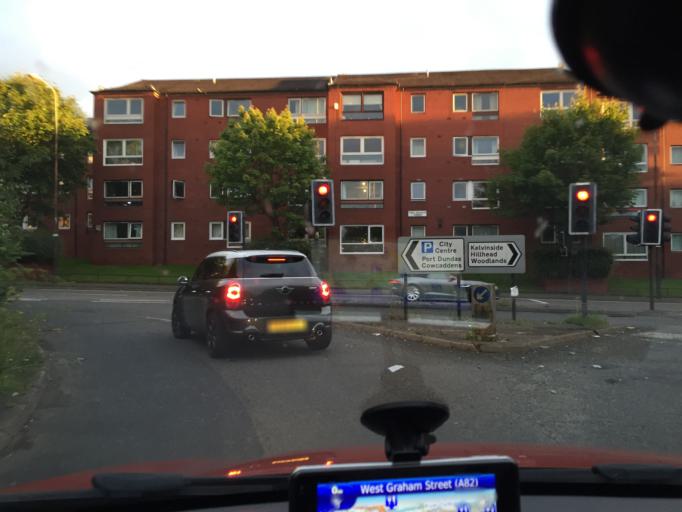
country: GB
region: Scotland
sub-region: Glasgow City
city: Glasgow
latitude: 55.8689
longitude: -4.2658
